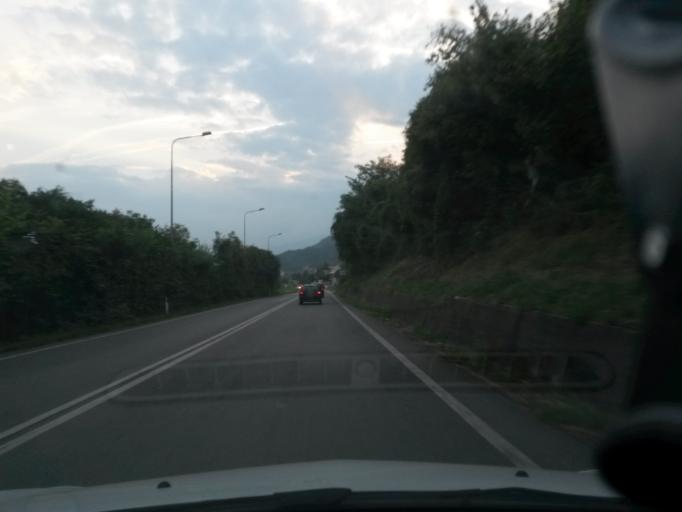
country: IT
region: Piedmont
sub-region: Provincia di Torino
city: Caselette
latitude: 45.1064
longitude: 7.4915
